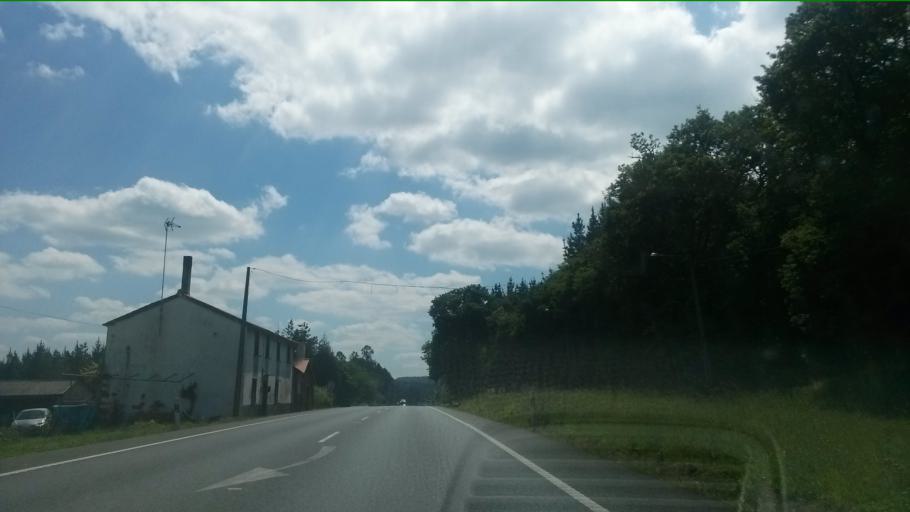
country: ES
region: Galicia
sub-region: Provincia da Coruna
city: Touro
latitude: 42.9554
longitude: -8.3238
